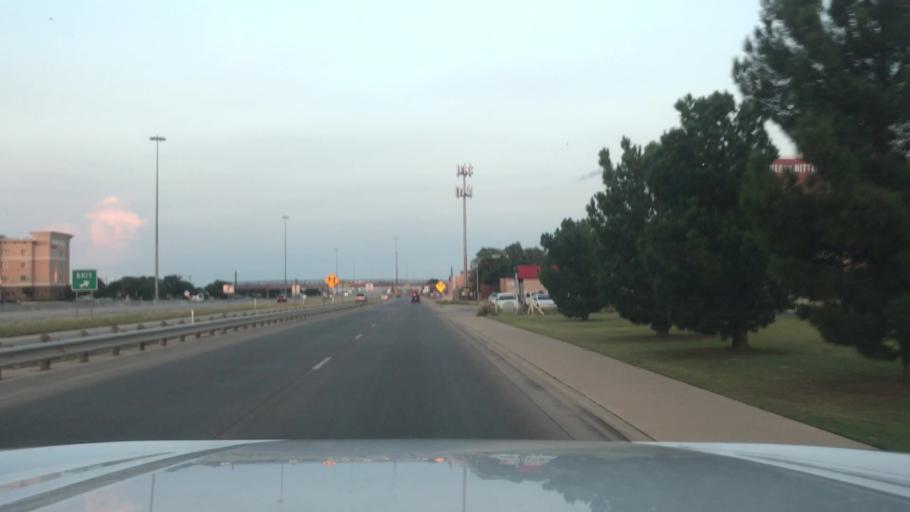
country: US
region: Texas
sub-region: Lubbock County
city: Lubbock
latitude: 33.5923
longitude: -101.8674
